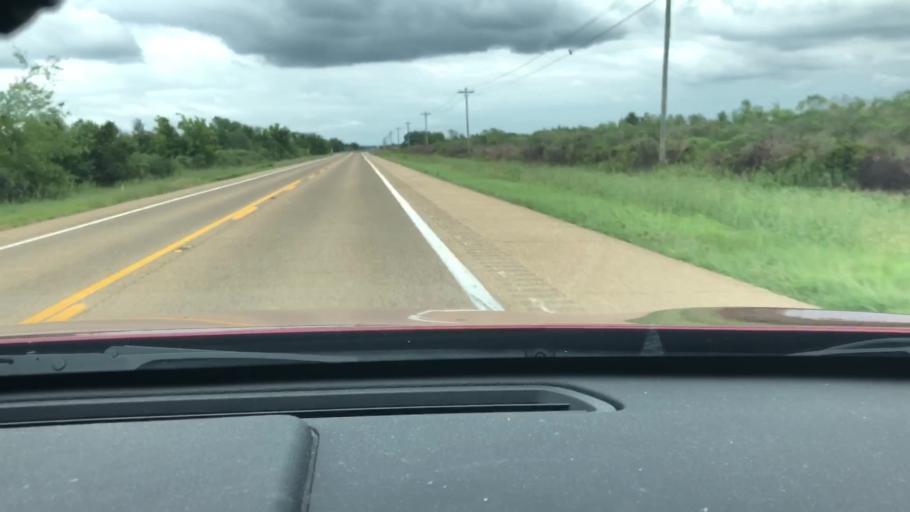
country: US
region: Arkansas
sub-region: Lafayette County
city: Lewisville
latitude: 33.4126
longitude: -93.8034
